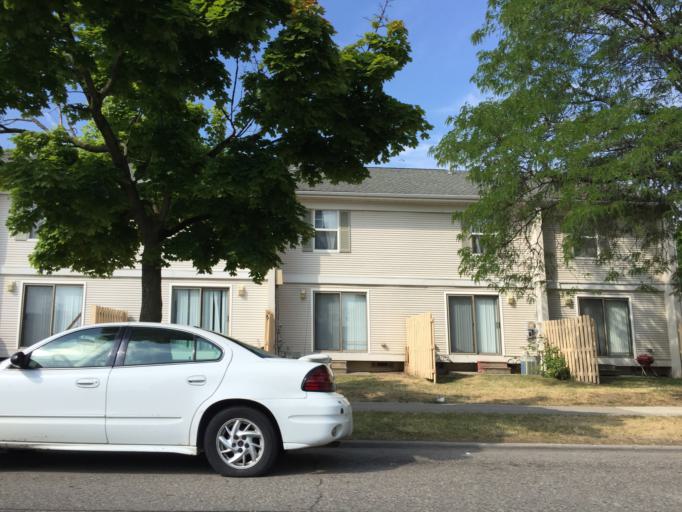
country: US
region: Michigan
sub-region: Wayne County
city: Detroit
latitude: 42.3401
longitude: -83.0241
